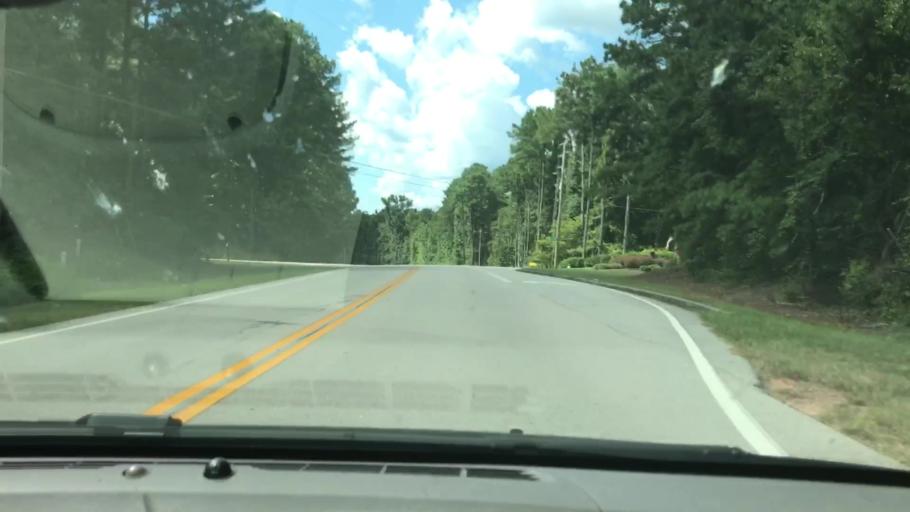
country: US
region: Georgia
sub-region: Troup County
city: La Grange
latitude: 33.0985
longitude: -85.0624
